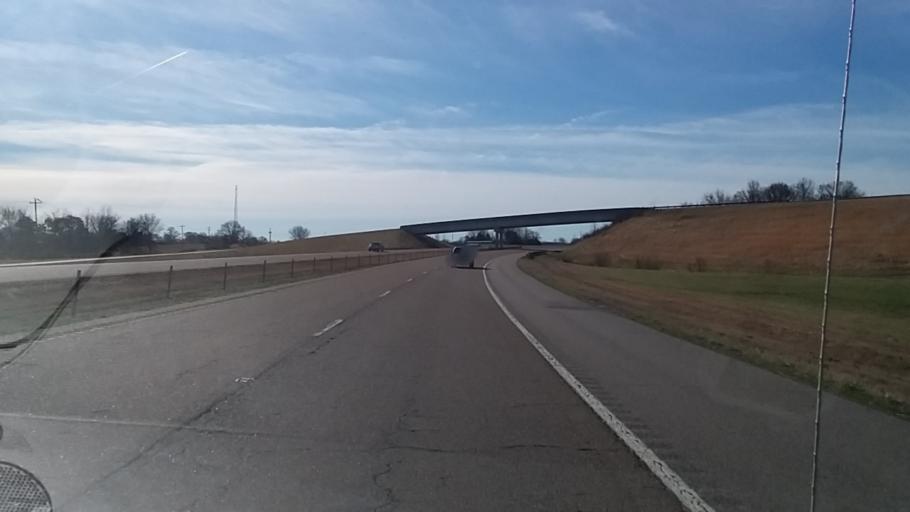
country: US
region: Tennessee
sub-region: Crockett County
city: Alamo
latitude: 35.8139
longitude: -89.1622
